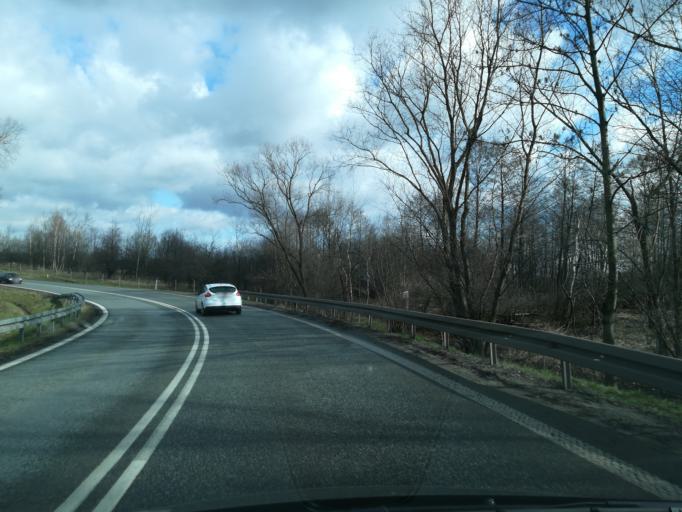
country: PL
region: Lesser Poland Voivodeship
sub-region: Powiat krakowski
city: Balice
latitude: 50.0725
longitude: 19.8114
